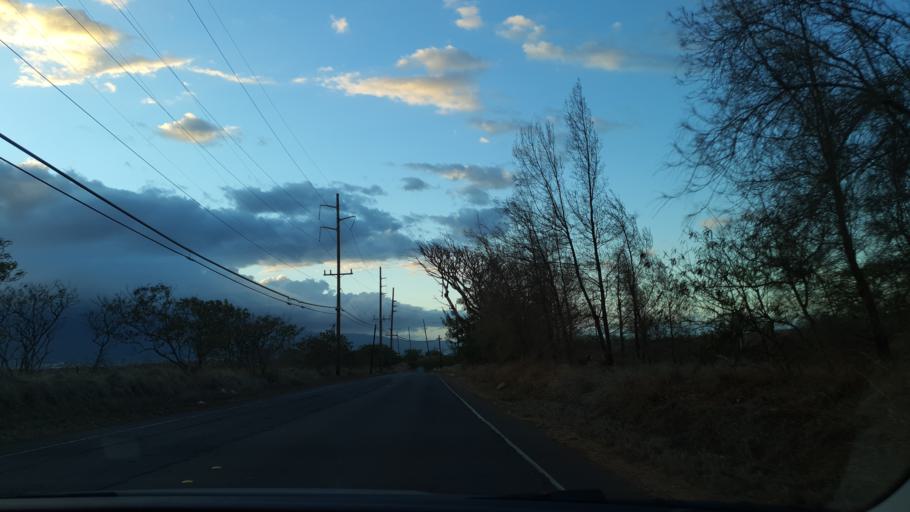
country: US
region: Hawaii
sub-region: Maui County
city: Kahului
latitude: 20.8693
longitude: -156.4360
